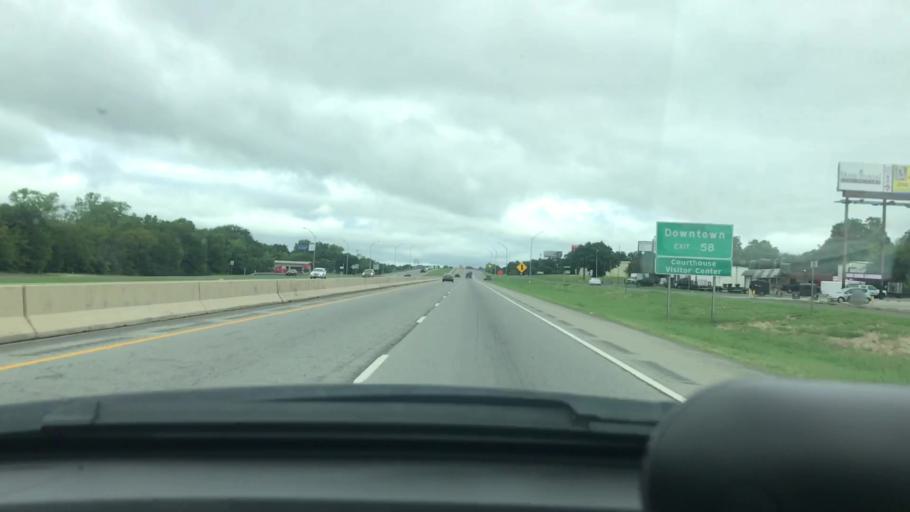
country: US
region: Texas
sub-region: Grayson County
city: Sherman
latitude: 33.6236
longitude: -96.6120
